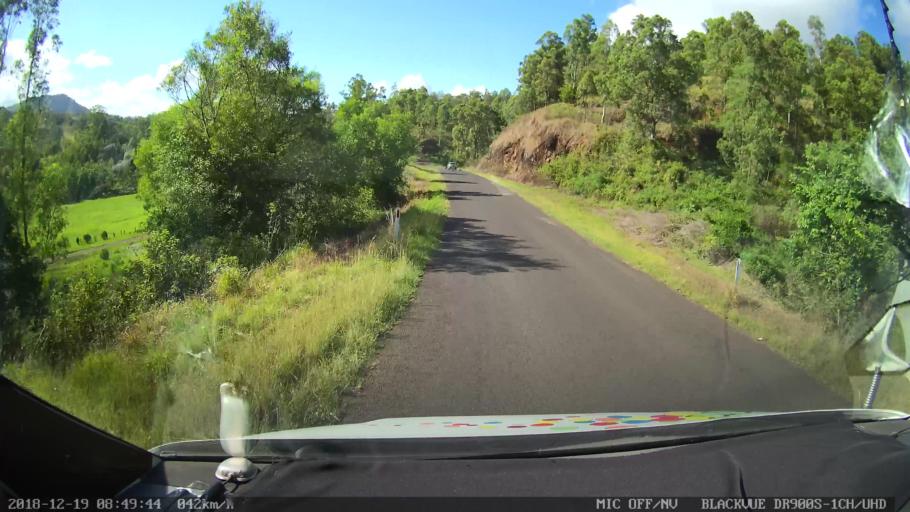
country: AU
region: New South Wales
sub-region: Kyogle
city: Kyogle
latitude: -28.3770
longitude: 152.9731
